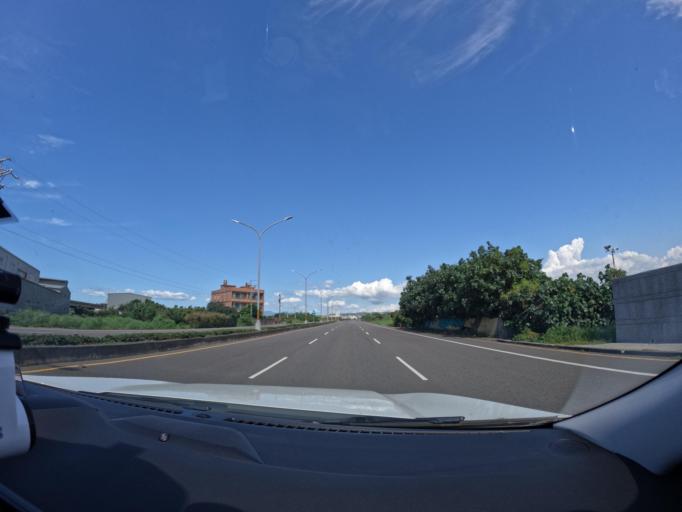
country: TW
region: Taiwan
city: Taoyuan City
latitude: 25.1077
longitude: 121.2304
